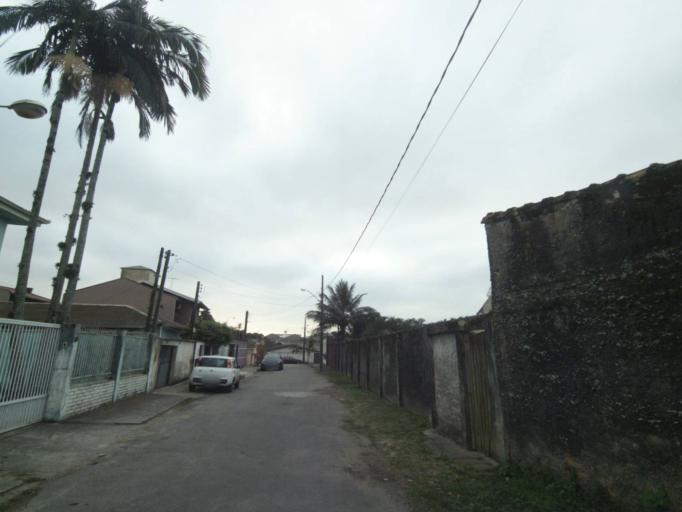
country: BR
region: Parana
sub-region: Paranagua
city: Paranagua
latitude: -25.5180
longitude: -48.5211
